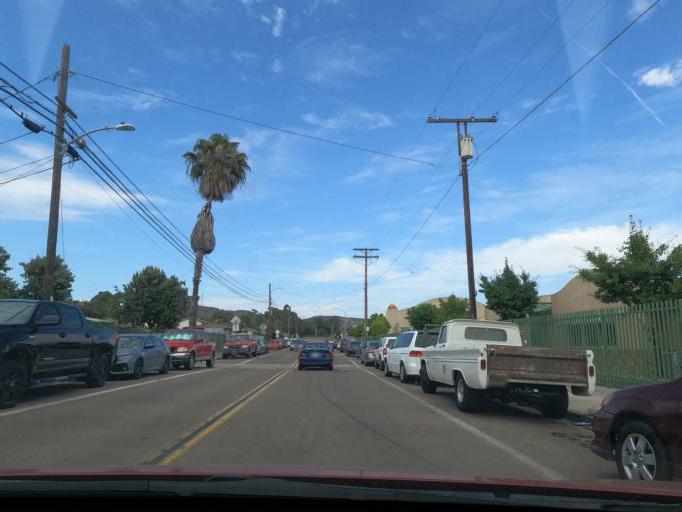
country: US
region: California
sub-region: San Diego County
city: Imperial Beach
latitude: 32.5582
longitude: -117.0513
